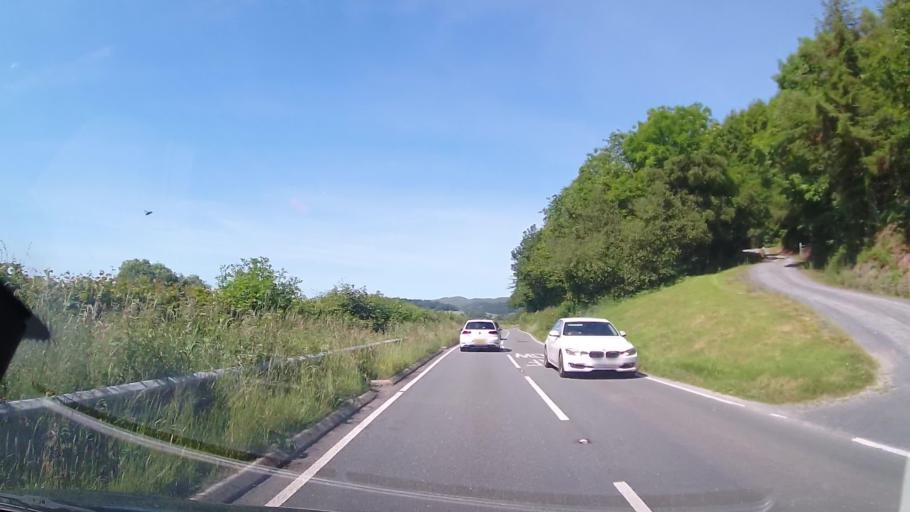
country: GB
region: Wales
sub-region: Sir Powys
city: Machynlleth
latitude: 52.5872
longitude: -3.9051
